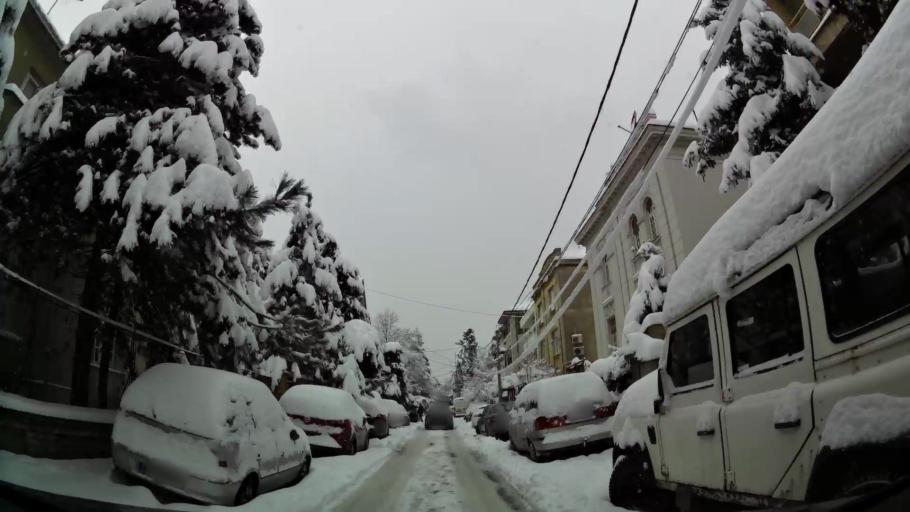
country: RS
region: Central Serbia
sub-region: Belgrade
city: Vracar
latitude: 44.7947
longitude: 20.4720
